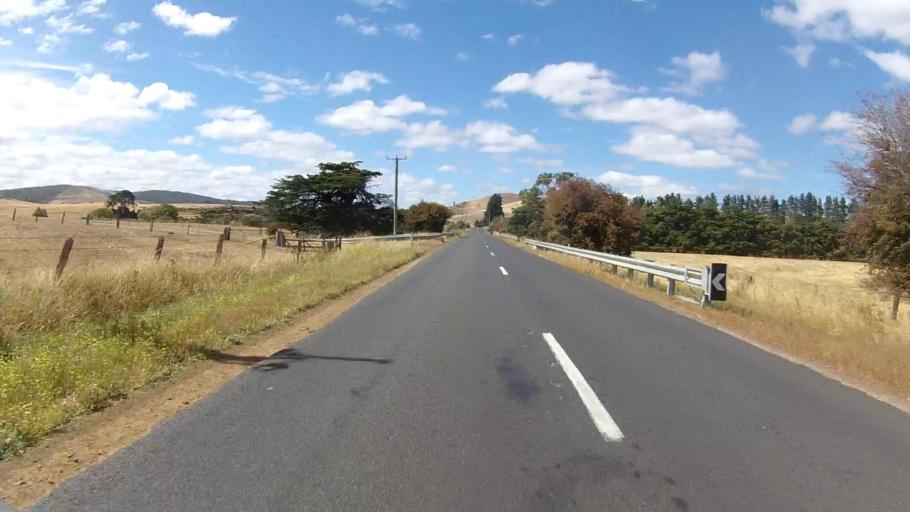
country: AU
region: Tasmania
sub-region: Brighton
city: Bridgewater
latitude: -42.5456
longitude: 147.3743
